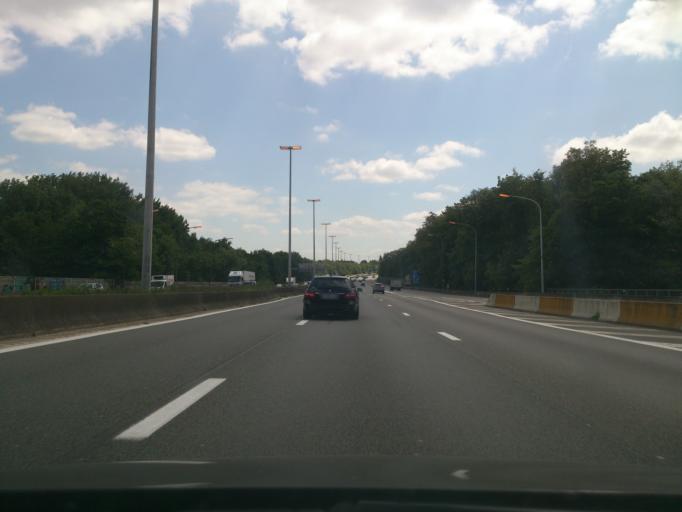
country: BE
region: Flanders
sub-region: Provincie Vlaams-Brabant
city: Kraainem
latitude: 50.8655
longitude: 4.4712
